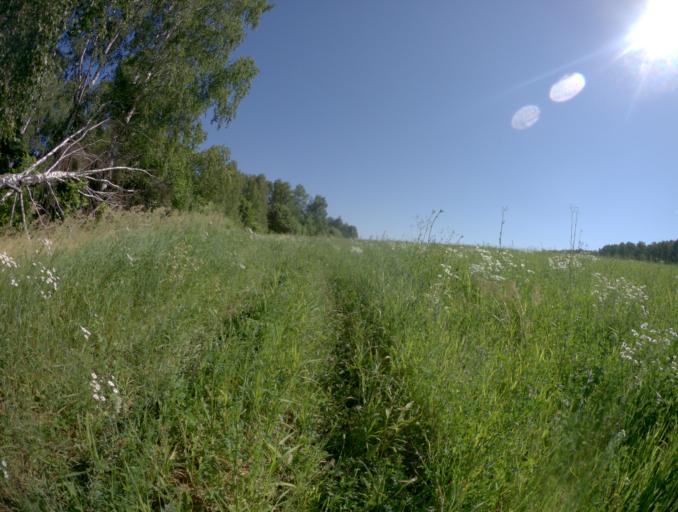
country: RU
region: Nizjnij Novgorod
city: Reshetikha
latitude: 56.1736
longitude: 43.3615
